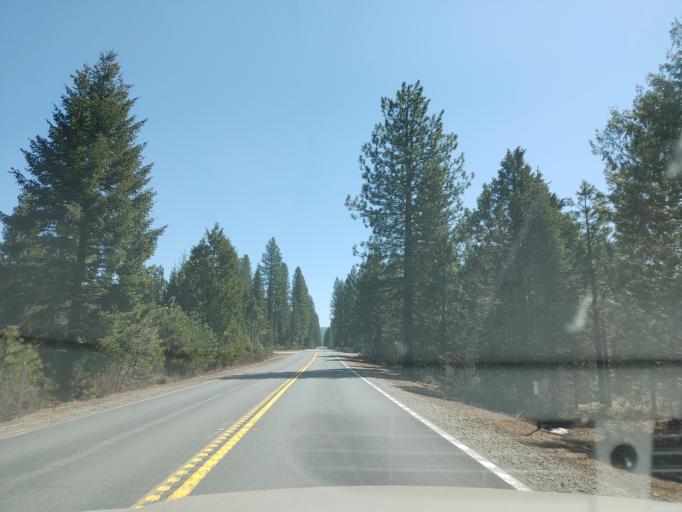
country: US
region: California
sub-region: Siskiyou County
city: McCloud
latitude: 41.2601
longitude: -121.8419
